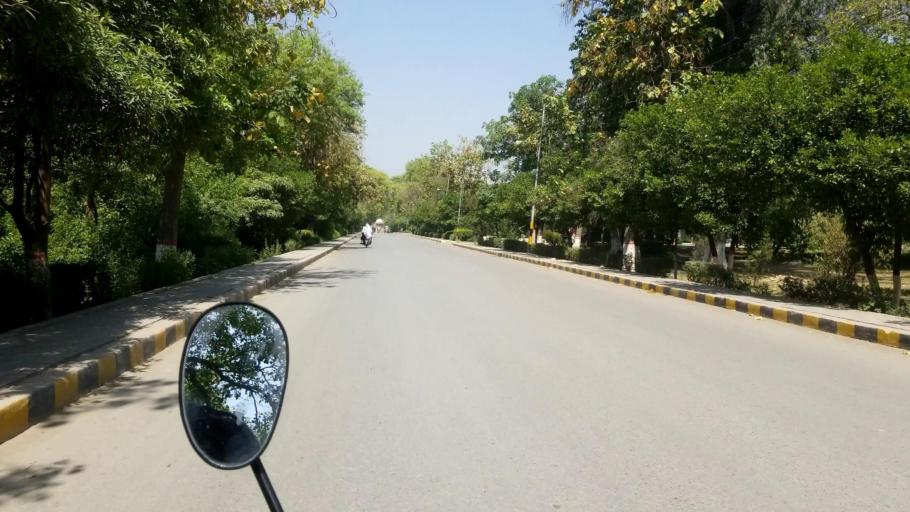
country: PK
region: Khyber Pakhtunkhwa
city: Peshawar
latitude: 34.0052
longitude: 71.4865
